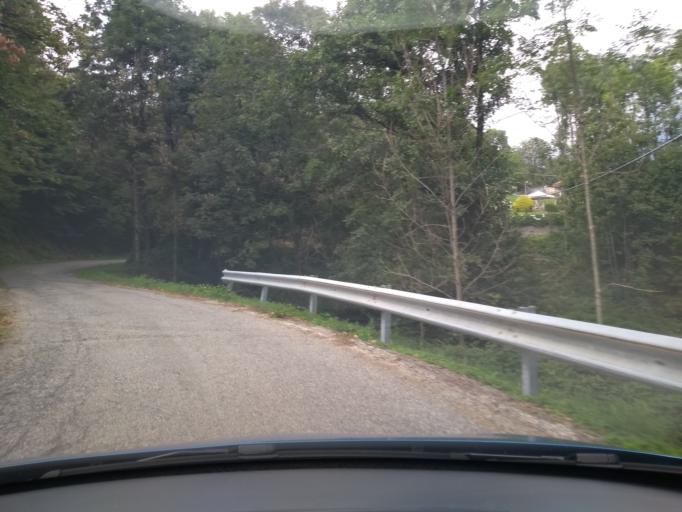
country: IT
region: Piedmont
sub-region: Provincia di Torino
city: Corio
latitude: 45.3343
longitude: 7.5176
